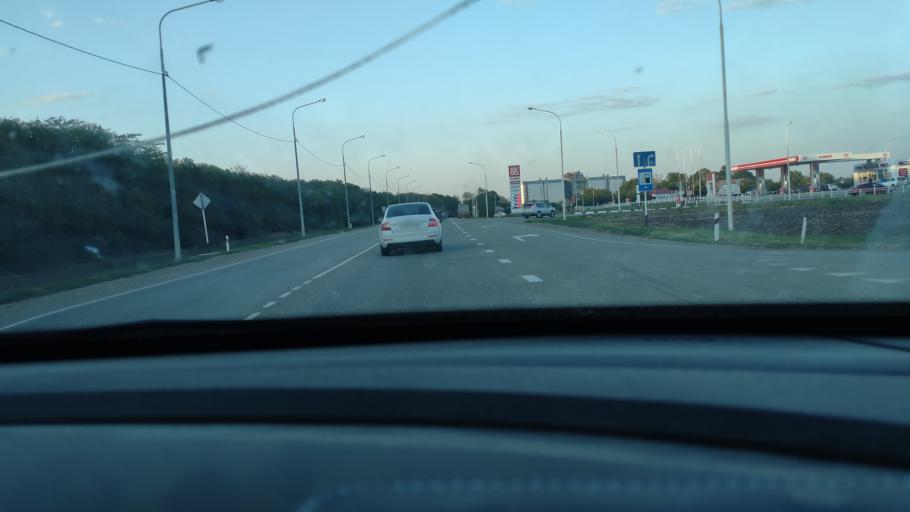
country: RU
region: Krasnodarskiy
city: Novominskaya
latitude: 46.3195
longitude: 38.9319
